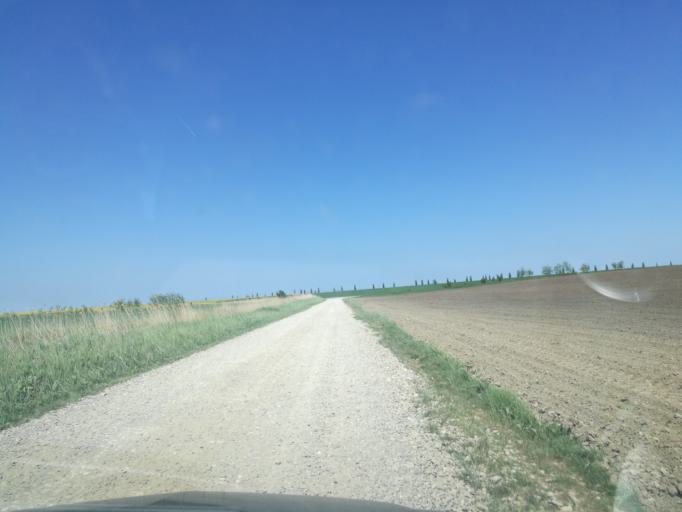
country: RO
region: Ialomita
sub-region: Comuna Adancata
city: Adancata
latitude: 44.7846
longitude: 26.4636
